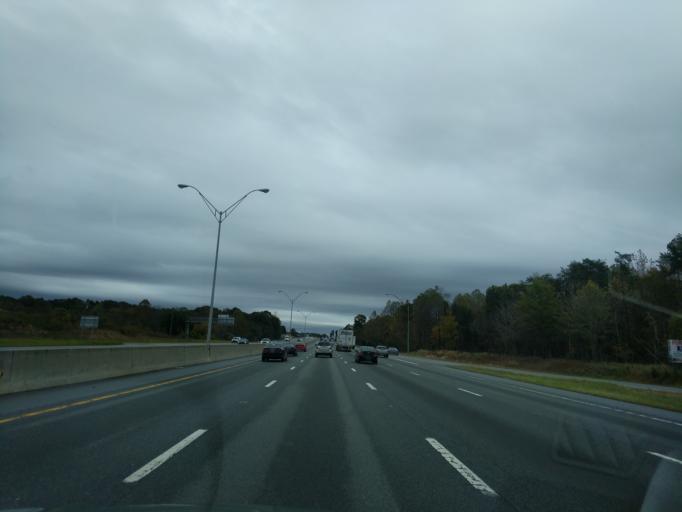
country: US
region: North Carolina
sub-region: Guilford County
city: Gibsonville
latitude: 36.0618
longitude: -79.5646
